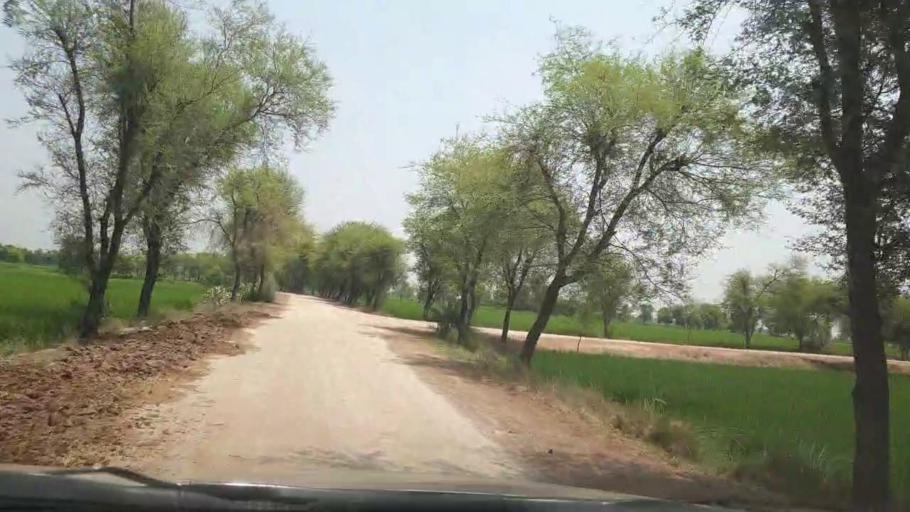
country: PK
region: Sindh
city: Ratodero
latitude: 27.7340
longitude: 68.2957
